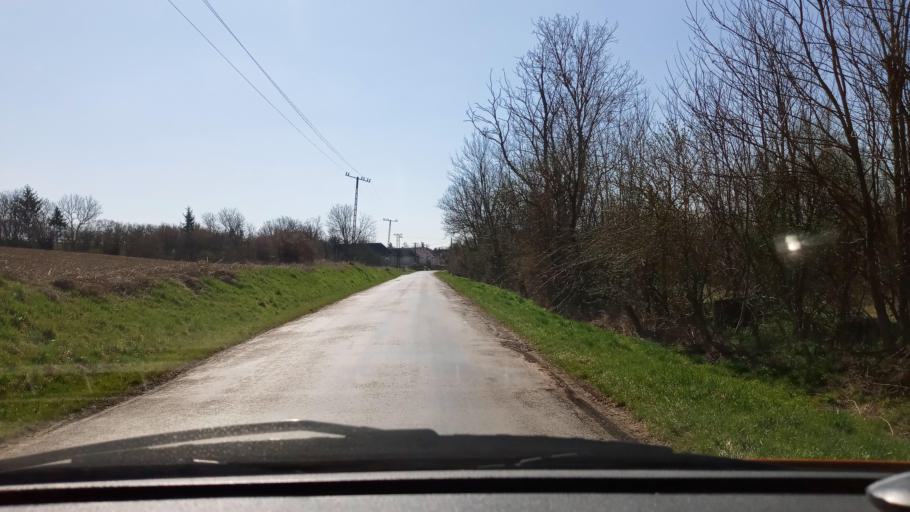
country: HU
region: Baranya
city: Kozarmisleny
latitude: 46.0645
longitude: 18.3720
